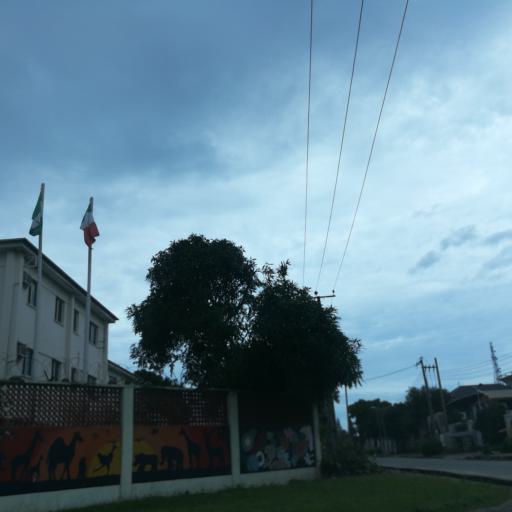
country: NG
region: Lagos
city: Ikoyi
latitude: 6.4455
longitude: 3.4650
